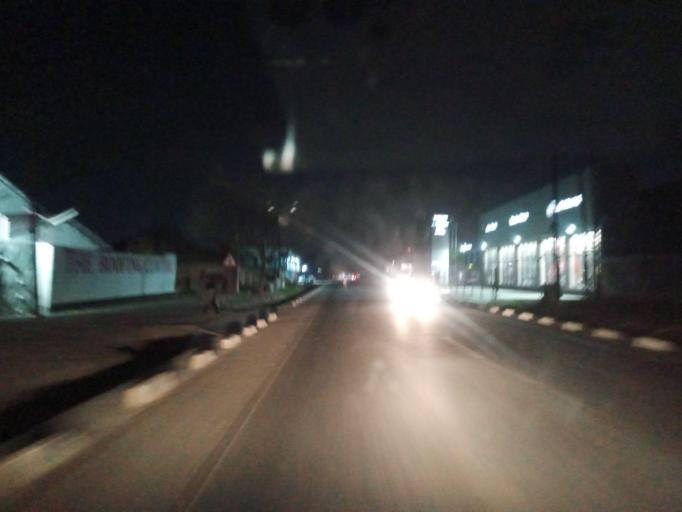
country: ZM
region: Lusaka
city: Lusaka
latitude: -15.3933
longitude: 28.2717
